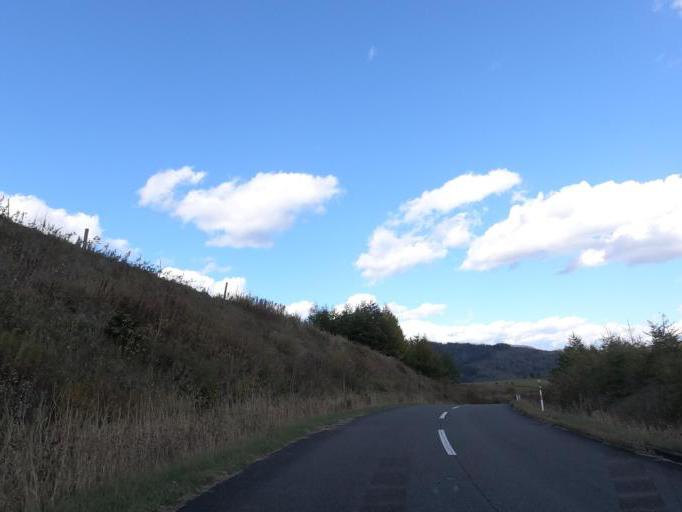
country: JP
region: Hokkaido
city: Otofuke
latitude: 43.2914
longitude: 143.1856
